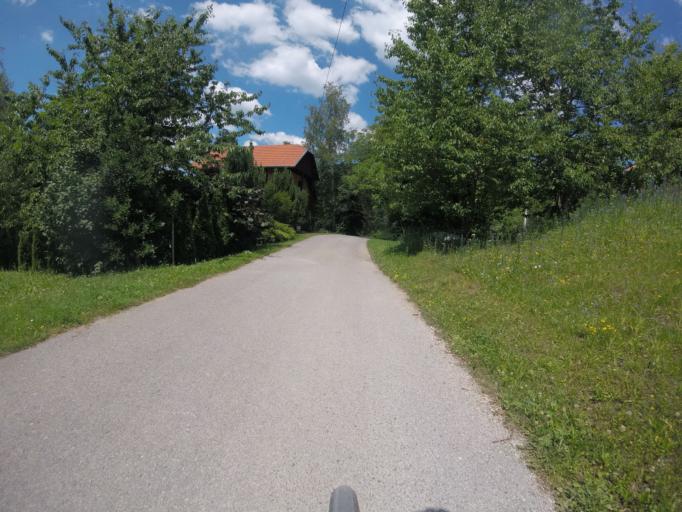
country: SI
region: Kostanjevica na Krki
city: Kostanjevica na Krki
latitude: 45.7568
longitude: 15.3983
